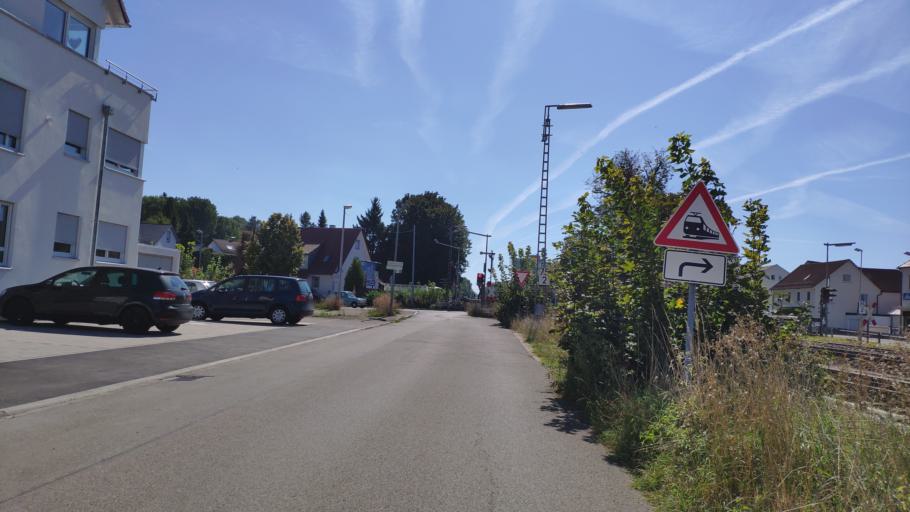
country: DE
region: Bavaria
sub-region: Swabia
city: Senden
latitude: 48.3258
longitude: 10.0491
